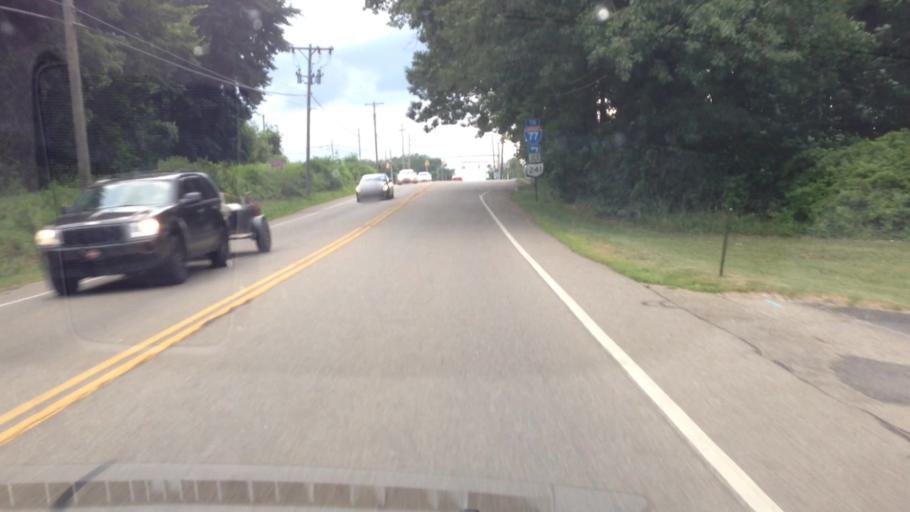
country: US
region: Ohio
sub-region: Summit County
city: Green
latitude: 40.9737
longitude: -81.4621
